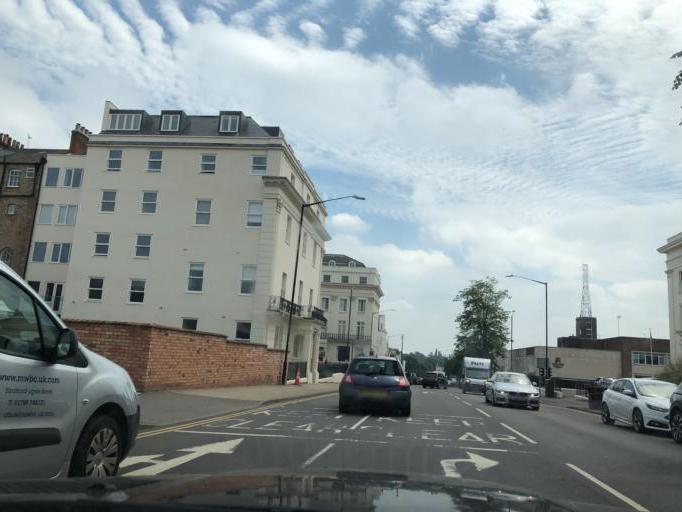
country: GB
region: England
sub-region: Warwickshire
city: Royal Leamington Spa
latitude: 52.2924
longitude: -1.5399
